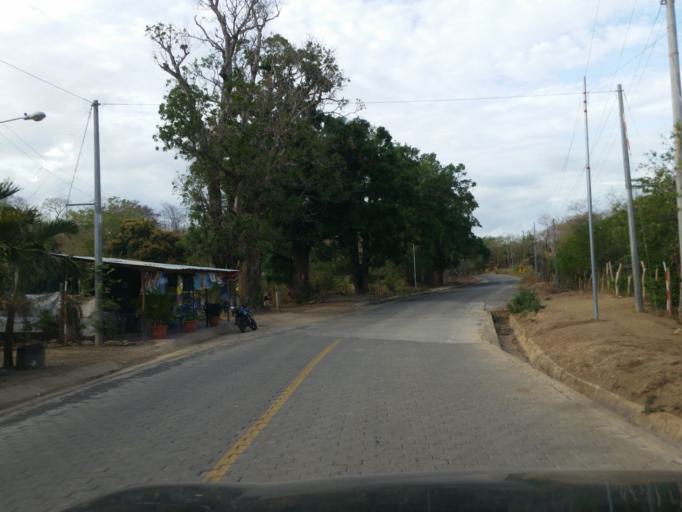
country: NI
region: Rivas
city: Tola
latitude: 11.4188
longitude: -85.9486
